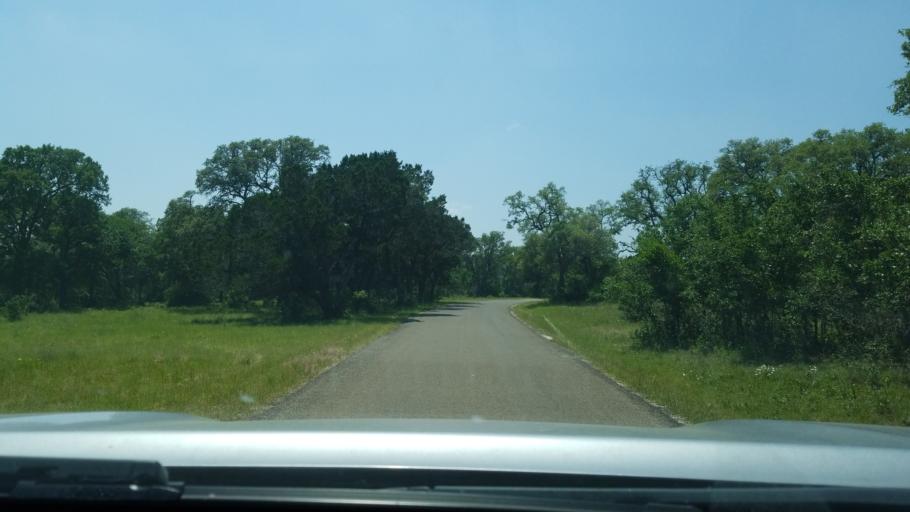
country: US
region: Texas
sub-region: Blanco County
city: Blanco
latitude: 30.0132
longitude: -98.4410
